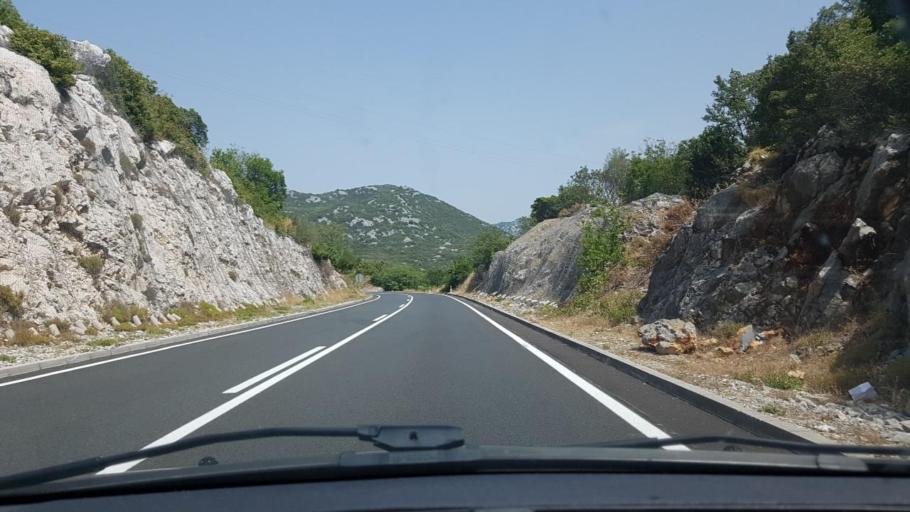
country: BA
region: Federation of Bosnia and Herzegovina
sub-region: Hercegovacko-Bosanski Kanton
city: Neum
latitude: 42.9262
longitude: 17.6427
